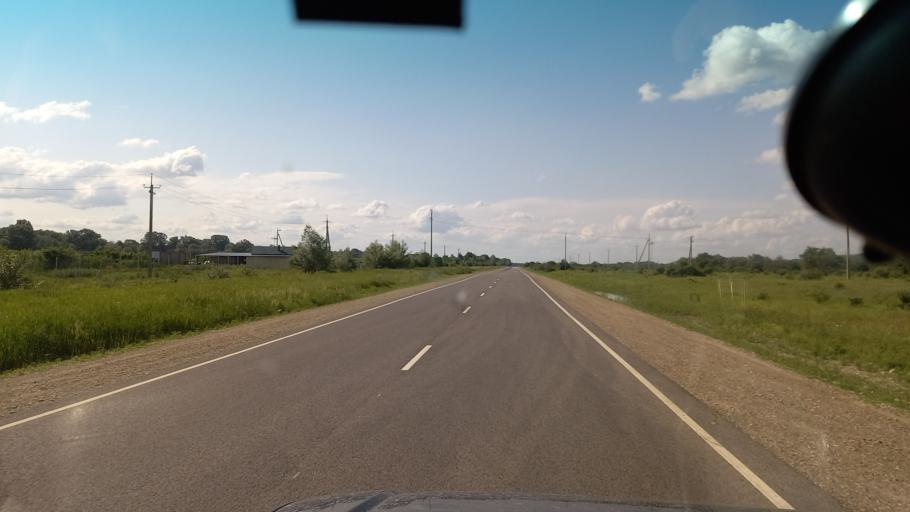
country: RU
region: Krasnodarskiy
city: Mostovskoy
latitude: 44.3898
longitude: 40.8471
